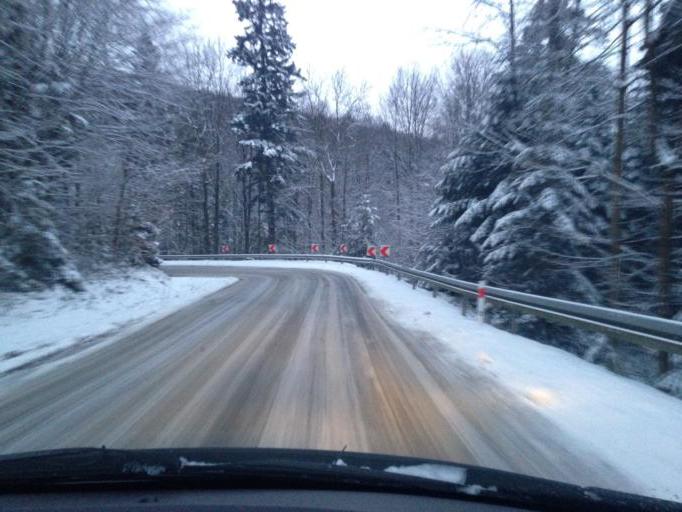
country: PL
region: Subcarpathian Voivodeship
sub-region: Powiat jasielski
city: Krempna
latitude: 49.5304
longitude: 21.5000
